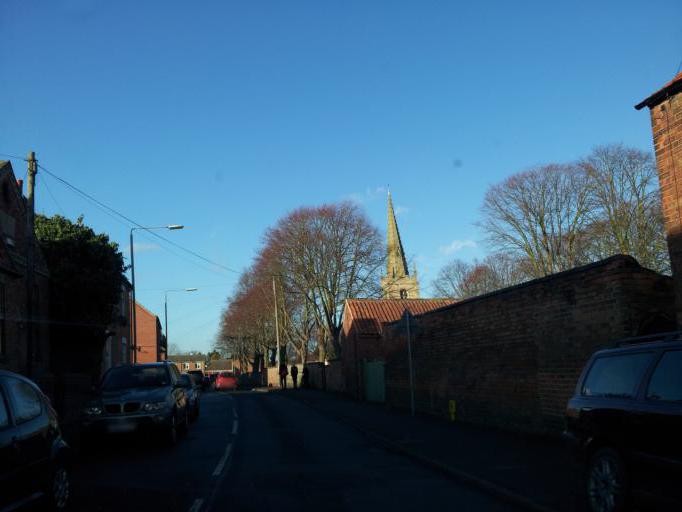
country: GB
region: England
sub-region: Nottinghamshire
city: Newark on Trent
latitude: 53.0542
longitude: -0.7788
